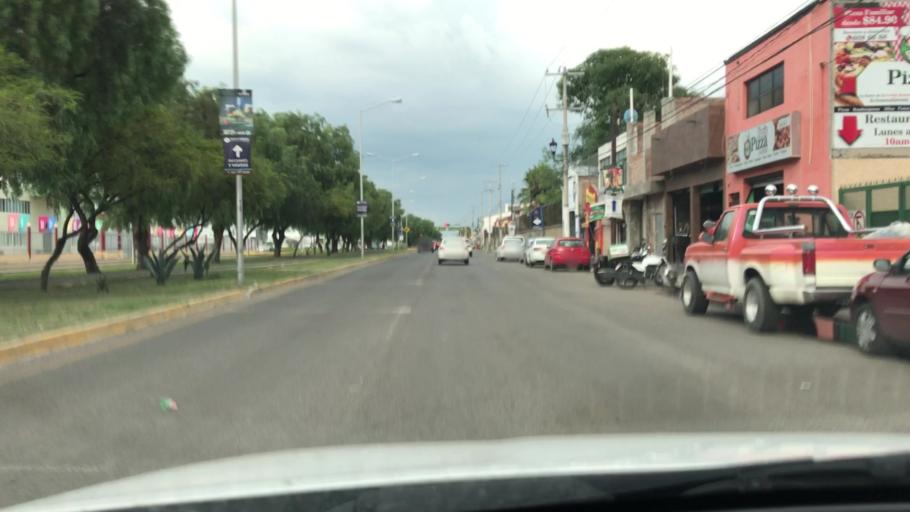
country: MX
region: Guanajuato
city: Celaya
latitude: 20.5363
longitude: -100.7938
